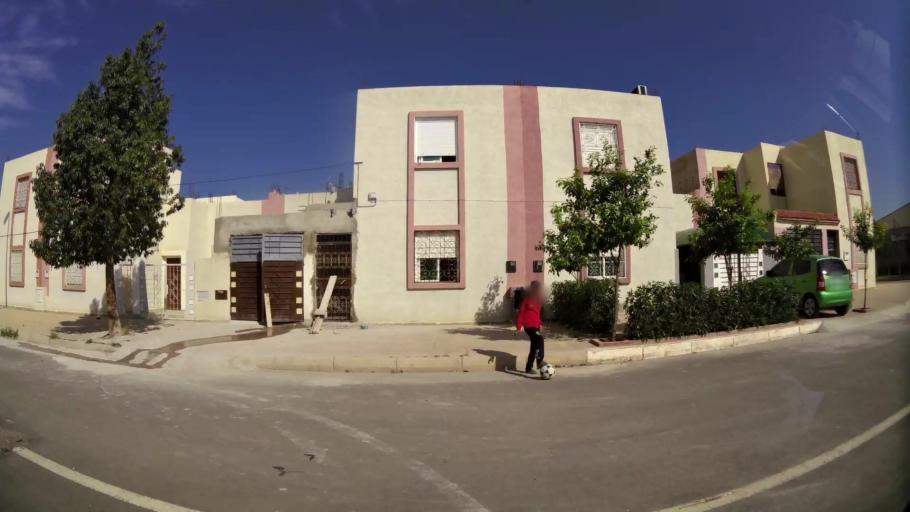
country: MA
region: Oriental
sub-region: Oujda-Angad
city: Oujda
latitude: 34.7084
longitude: -1.8833
